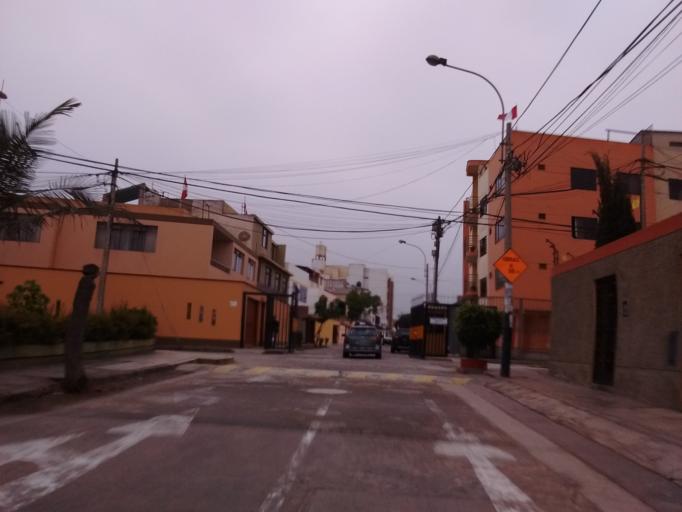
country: PE
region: Callao
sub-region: Callao
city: Callao
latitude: -12.0700
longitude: -77.0721
